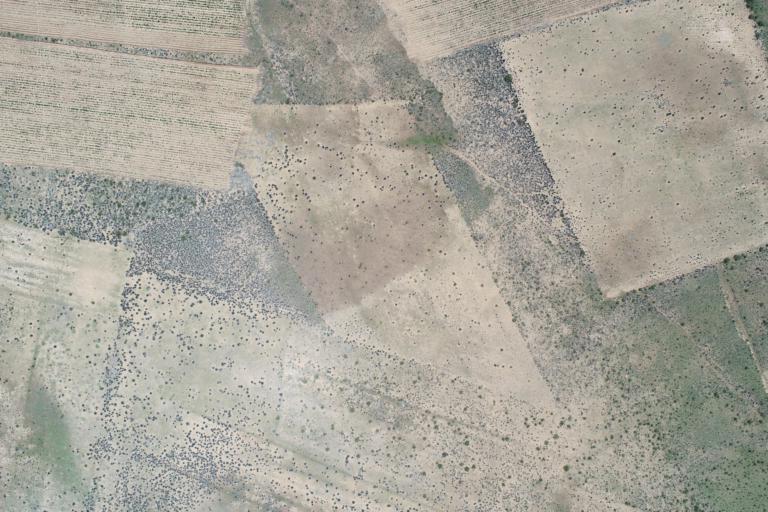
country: BO
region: La Paz
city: Curahuara de Carangas
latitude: -17.3110
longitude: -68.5091
